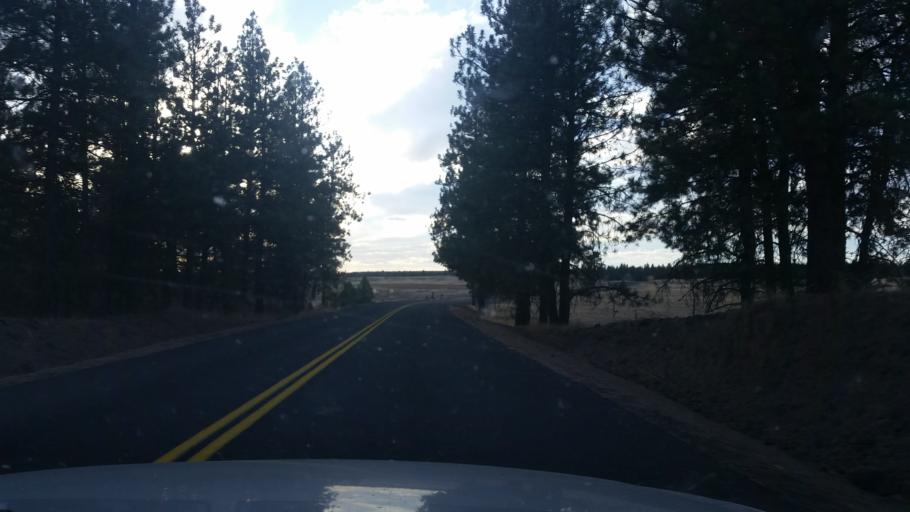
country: US
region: Washington
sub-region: Spokane County
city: Medical Lake
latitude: 47.4498
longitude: -117.7935
